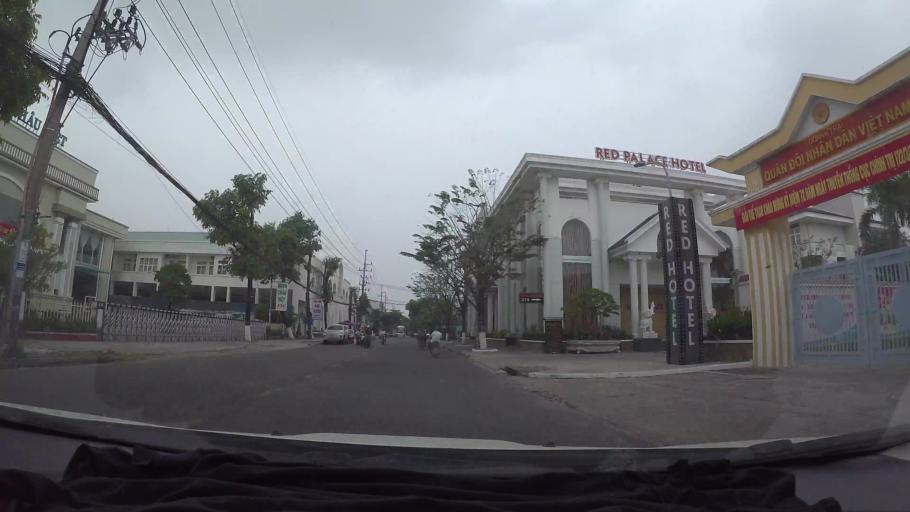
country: VN
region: Da Nang
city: Da Nang
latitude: 16.0514
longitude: 108.2121
